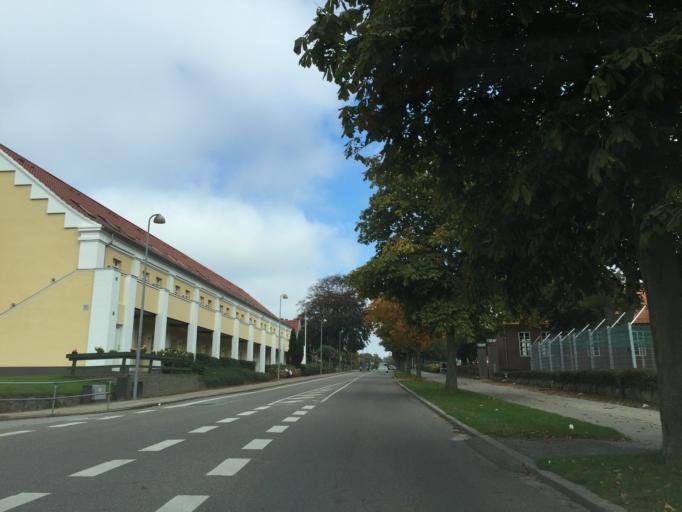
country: DK
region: South Denmark
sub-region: Sonderborg Kommune
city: Sonderborg
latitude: 54.9091
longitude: 9.7943
